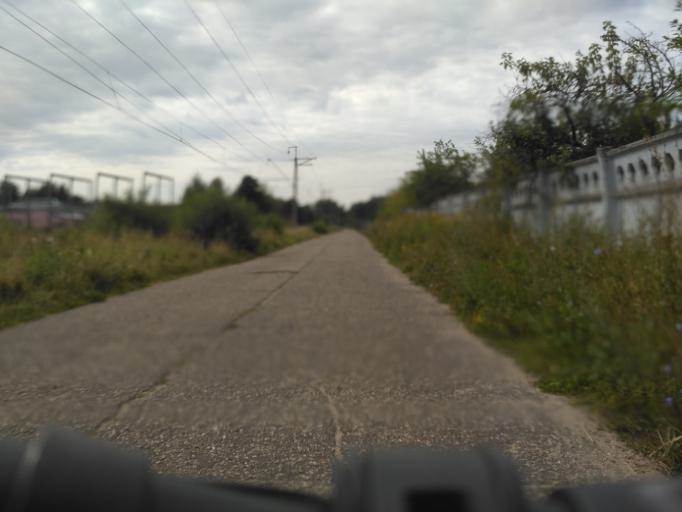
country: RU
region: Moskovskaya
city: Dubna
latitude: 56.7328
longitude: 37.1415
